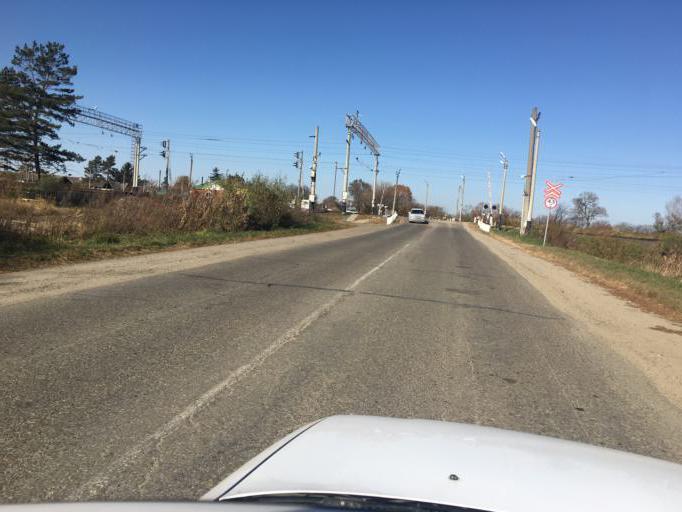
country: RU
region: Primorskiy
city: Dal'nerechensk
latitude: 45.9117
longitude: 133.7953
